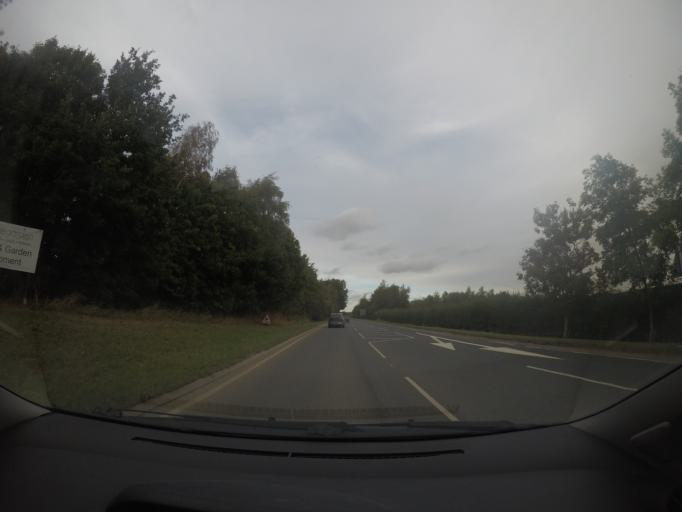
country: GB
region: England
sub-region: North Yorkshire
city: Riccall
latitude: 53.8541
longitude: -1.0497
